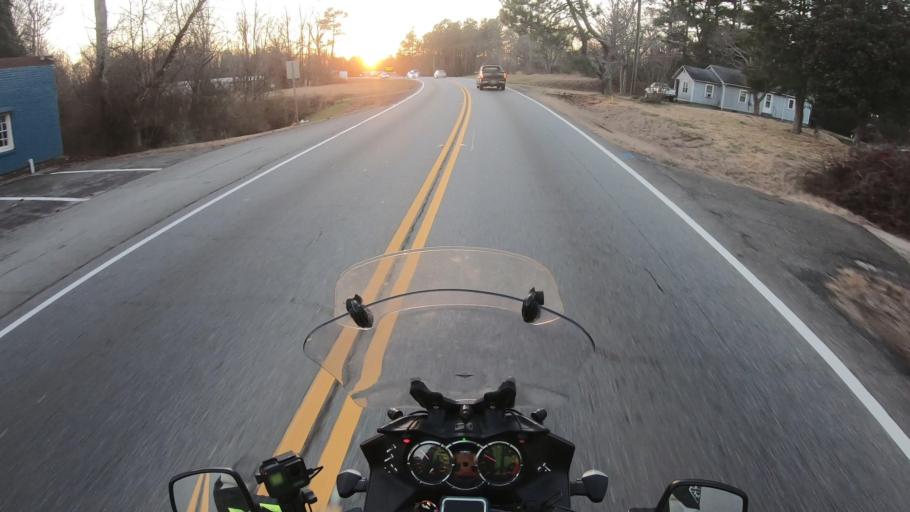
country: US
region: Georgia
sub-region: Cherokee County
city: Canton
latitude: 34.2406
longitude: -84.4272
